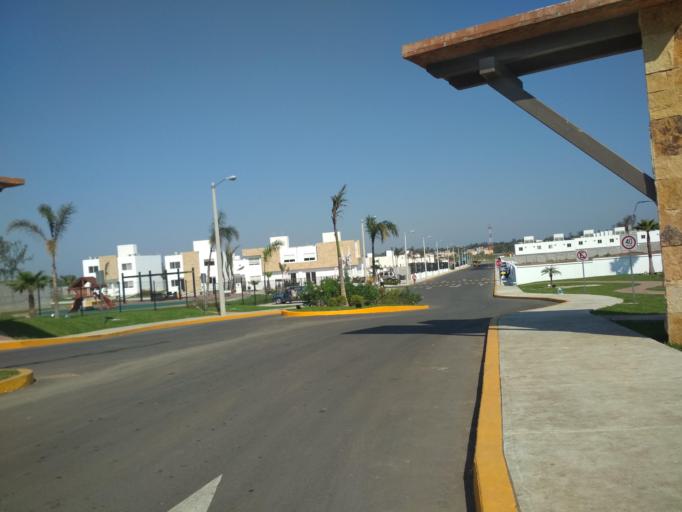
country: MX
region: Veracruz
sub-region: Veracruz
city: Las Amapolas
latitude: 19.1500
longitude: -96.2105
